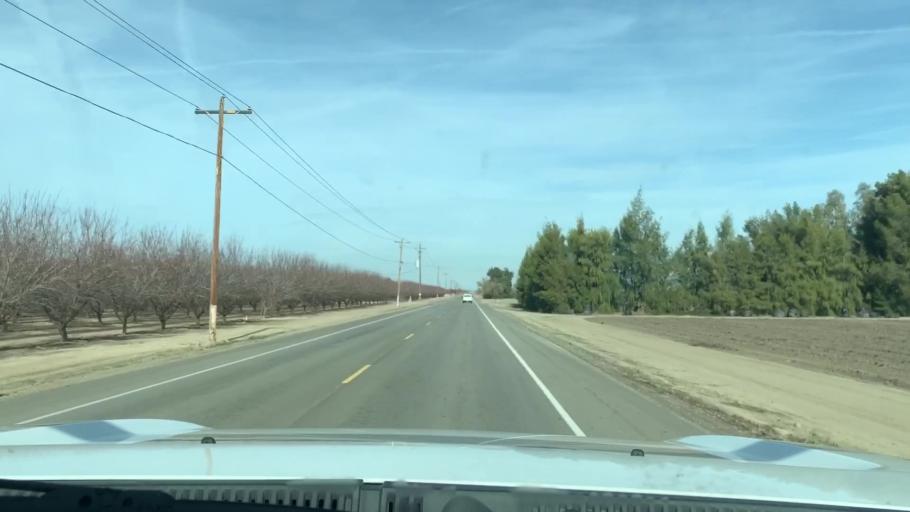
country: US
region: California
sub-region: Kern County
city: Buttonwillow
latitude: 35.5099
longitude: -119.4747
